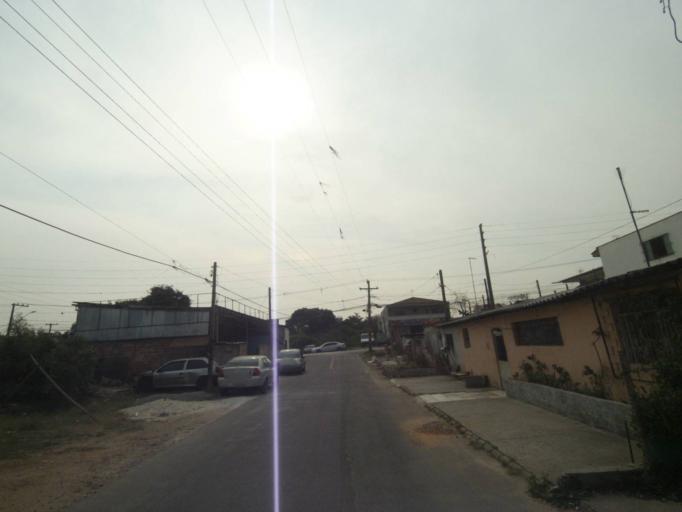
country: BR
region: Parana
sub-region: Sao Jose Dos Pinhais
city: Sao Jose dos Pinhais
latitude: -25.5225
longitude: -49.2799
